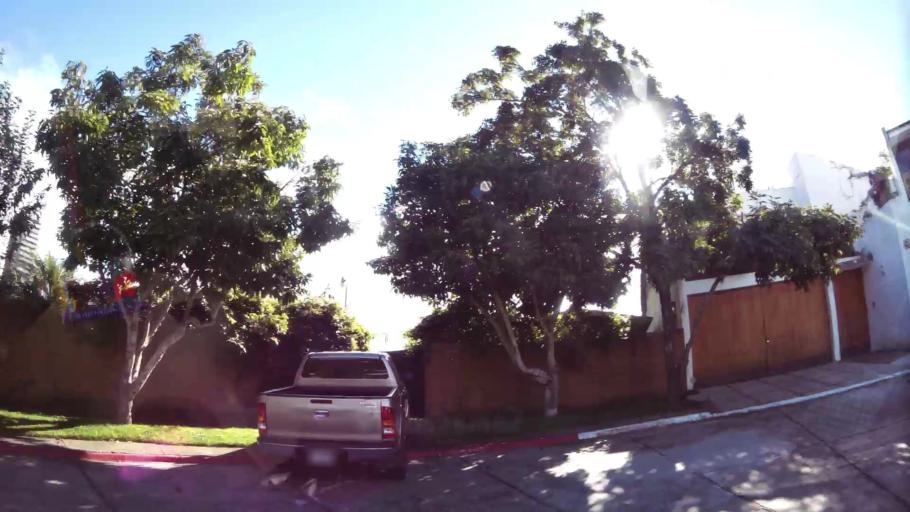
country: GT
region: Guatemala
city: Santa Catarina Pinula
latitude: 14.5692
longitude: -90.5252
